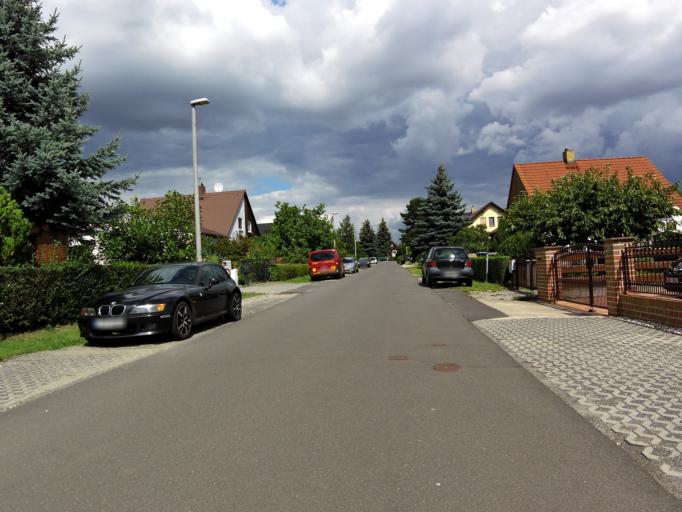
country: DE
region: Saxony
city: Rackwitz
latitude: 51.3838
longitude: 12.4116
